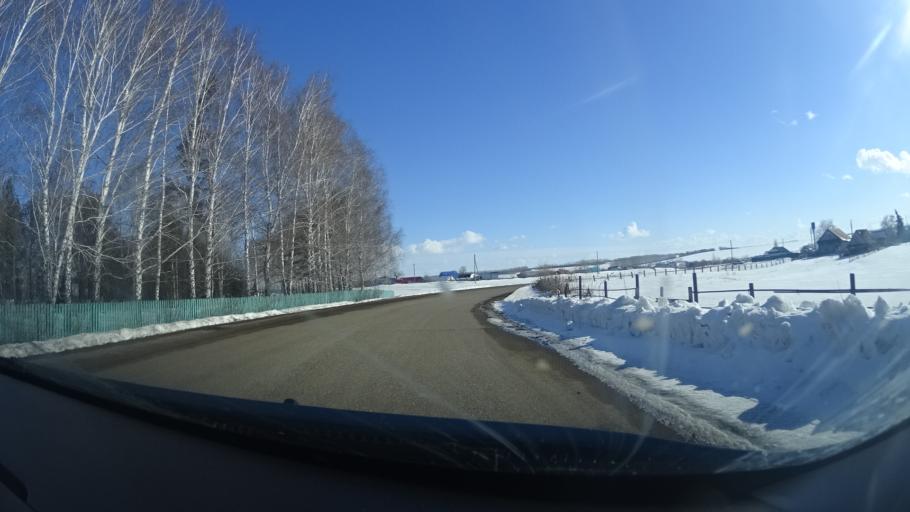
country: RU
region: Bashkortostan
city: Chishmy
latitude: 54.5977
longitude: 55.2573
